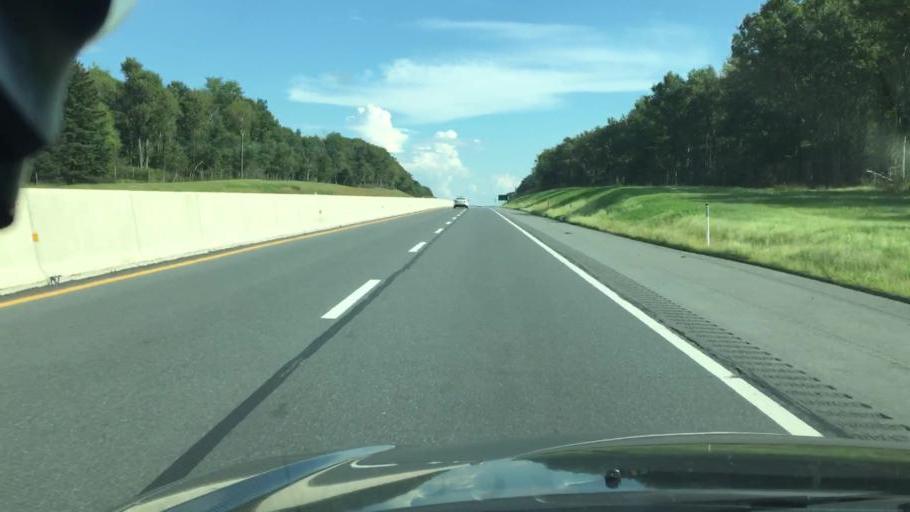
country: US
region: Pennsylvania
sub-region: Carbon County
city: Towamensing Trails
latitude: 41.0347
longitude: -75.6581
